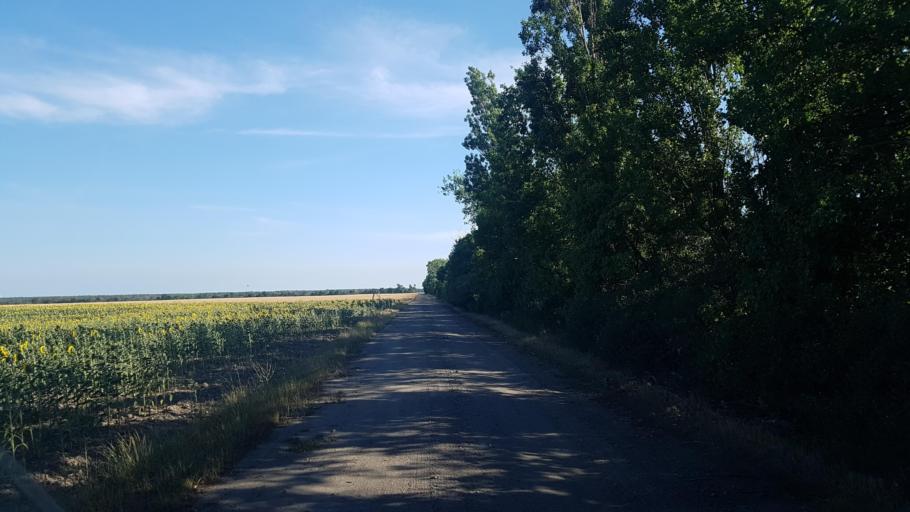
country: DE
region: Brandenburg
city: Muhlberg
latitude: 51.4329
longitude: 13.2864
